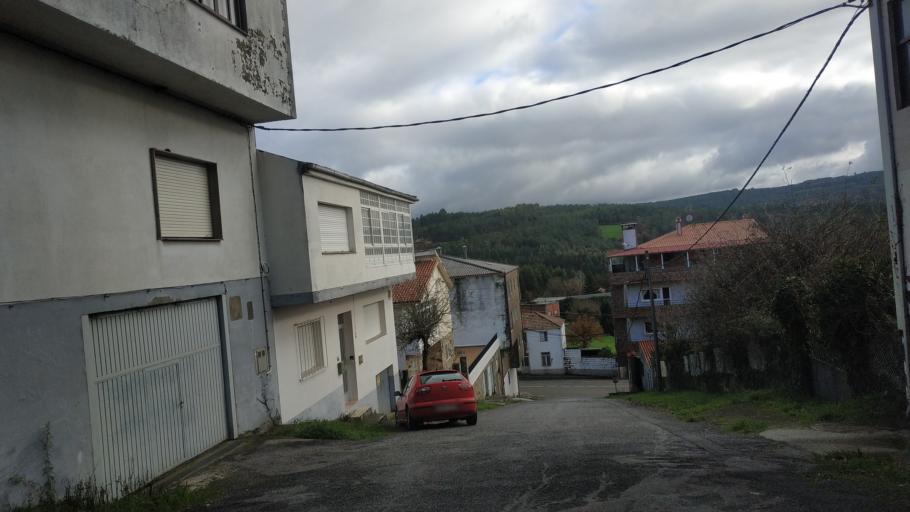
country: ES
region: Galicia
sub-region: Provincia de Pontevedra
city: Silleda
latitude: 42.7927
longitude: -8.1724
